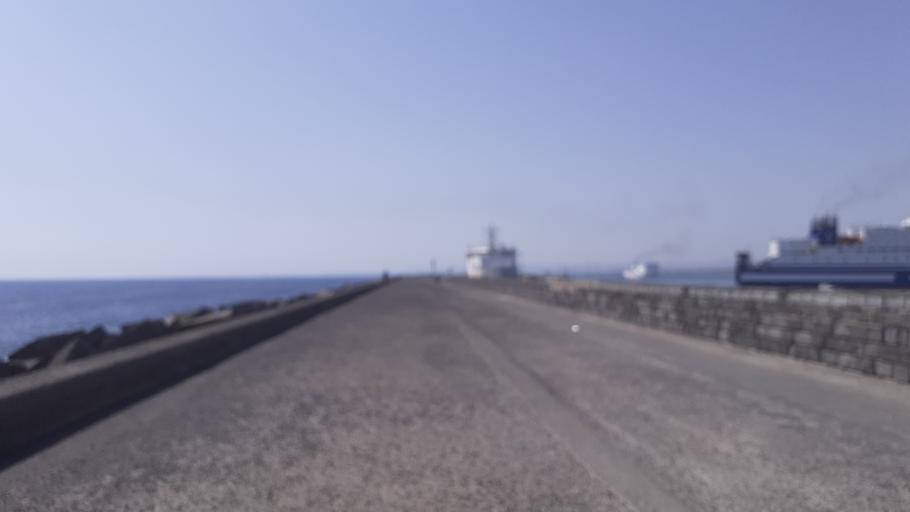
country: IT
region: Sicily
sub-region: Catania
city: Catania
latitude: 37.4966
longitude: 15.0994
